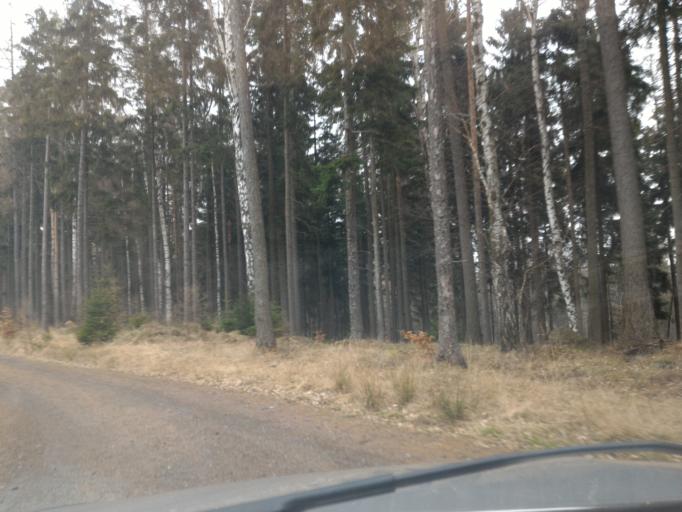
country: DE
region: Saxony
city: Olbersdorf
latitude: 50.8530
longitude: 14.7864
